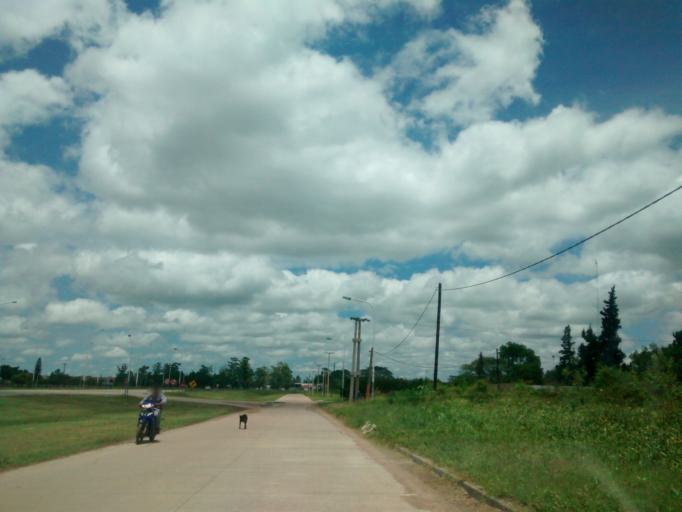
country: AR
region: Chaco
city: Fontana
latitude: -27.4101
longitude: -58.9910
